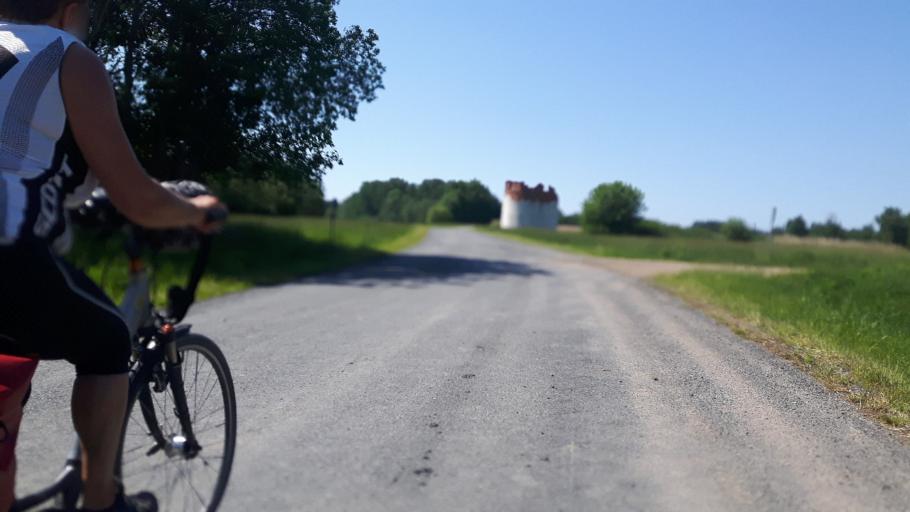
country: EE
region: Paernumaa
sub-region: Vaendra vald (alev)
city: Vandra
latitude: 58.5879
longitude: 25.0130
